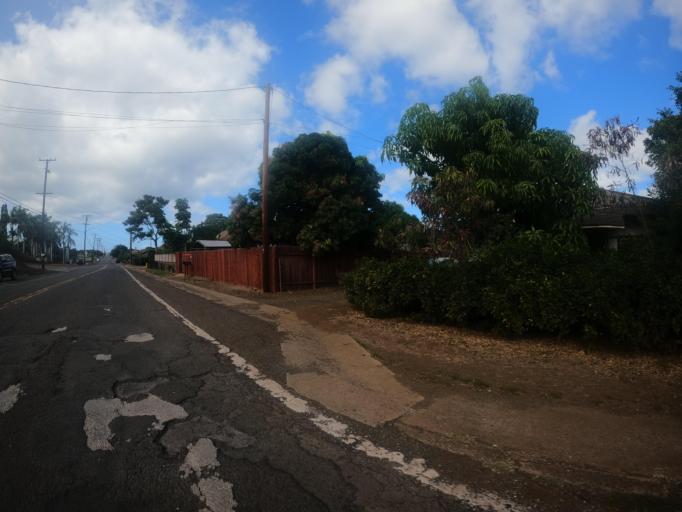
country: US
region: Hawaii
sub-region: Honolulu County
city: Waialua
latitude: 21.5676
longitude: -158.1276
